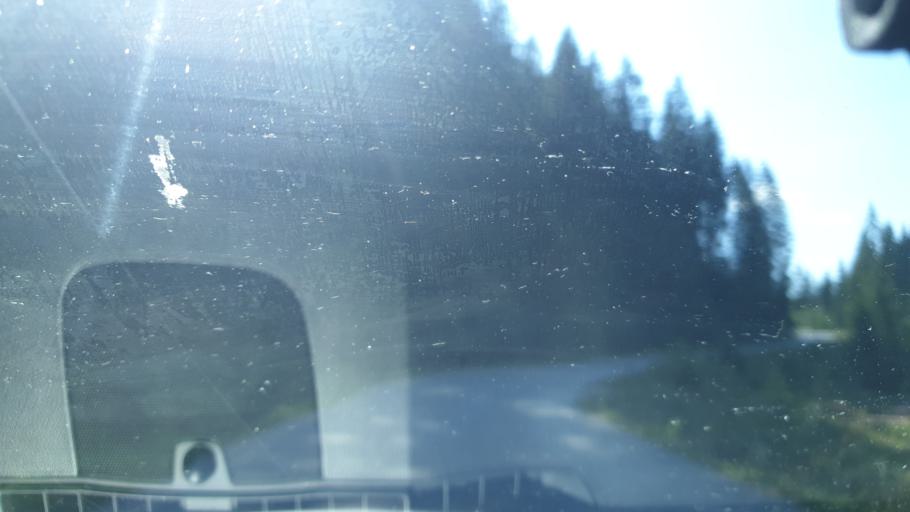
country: RS
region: Central Serbia
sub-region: Zlatiborski Okrug
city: Nova Varos
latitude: 43.4423
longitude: 19.8529
